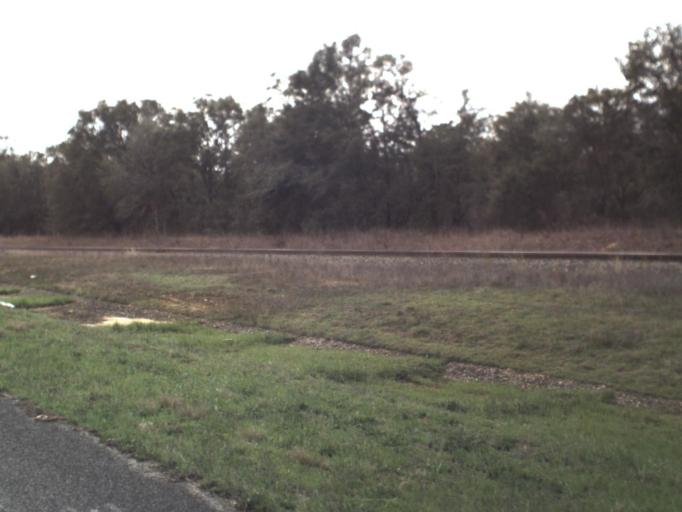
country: US
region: Florida
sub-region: Washington County
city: Chipley
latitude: 30.6402
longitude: -85.4000
